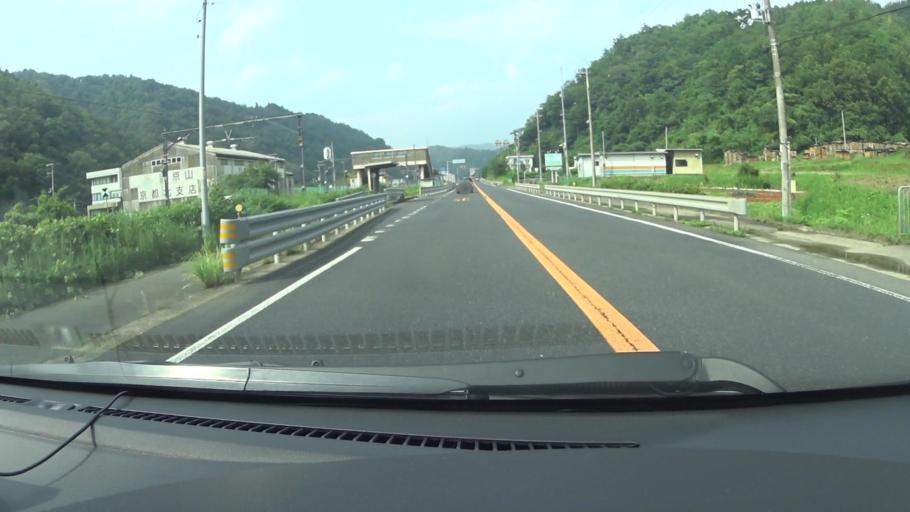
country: JP
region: Kyoto
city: Maizuru
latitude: 35.4059
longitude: 135.3253
